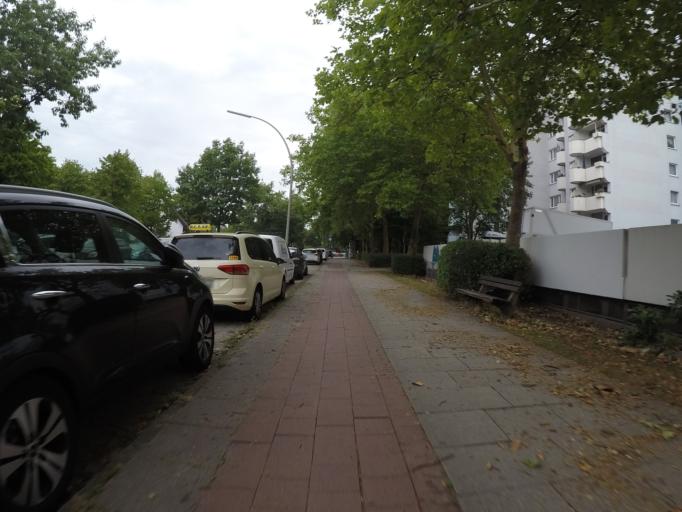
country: DE
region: Hamburg
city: Stellingen
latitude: 53.5851
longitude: 9.9479
